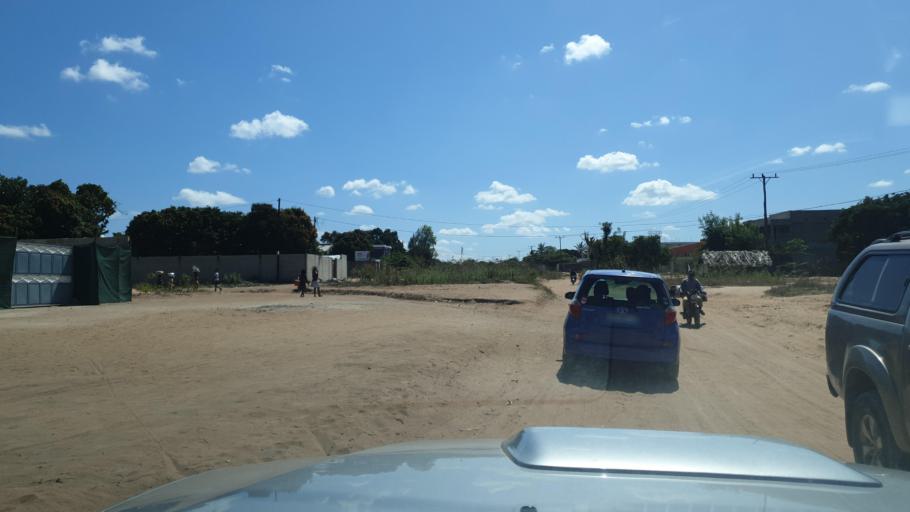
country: MZ
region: Nampula
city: Nampula
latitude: -15.1069
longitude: 39.2061
